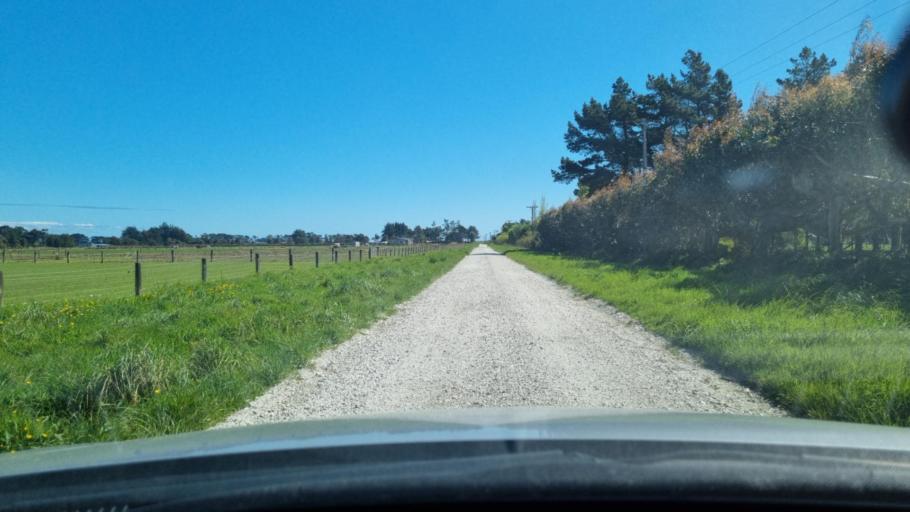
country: NZ
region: Southland
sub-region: Invercargill City
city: Invercargill
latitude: -46.3904
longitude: 168.3009
